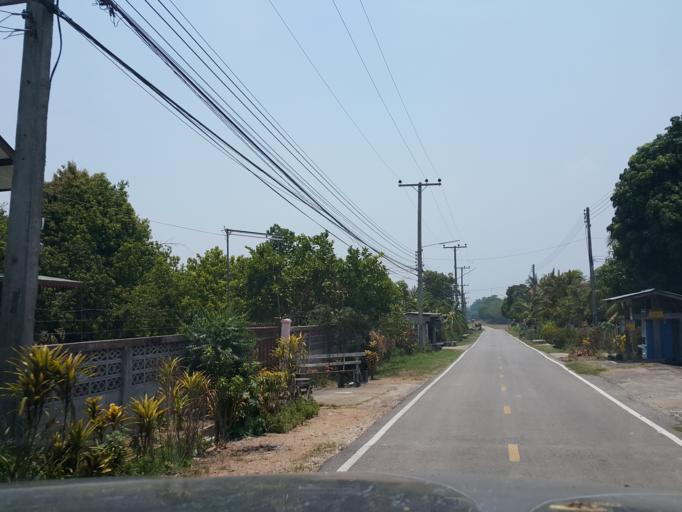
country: TH
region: Lampang
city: Thoen
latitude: 17.6372
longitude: 99.2656
